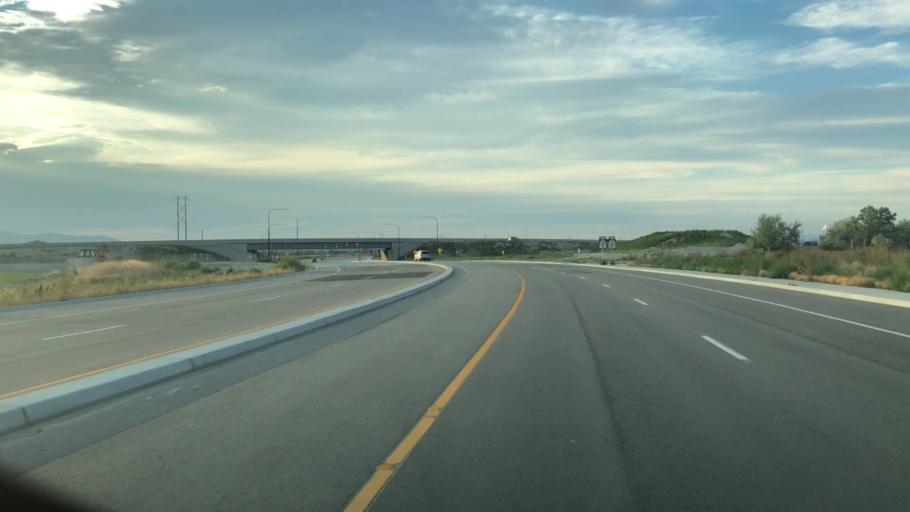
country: US
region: Utah
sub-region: Salt Lake County
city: Bluffdale
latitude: 40.4982
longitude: -111.9056
